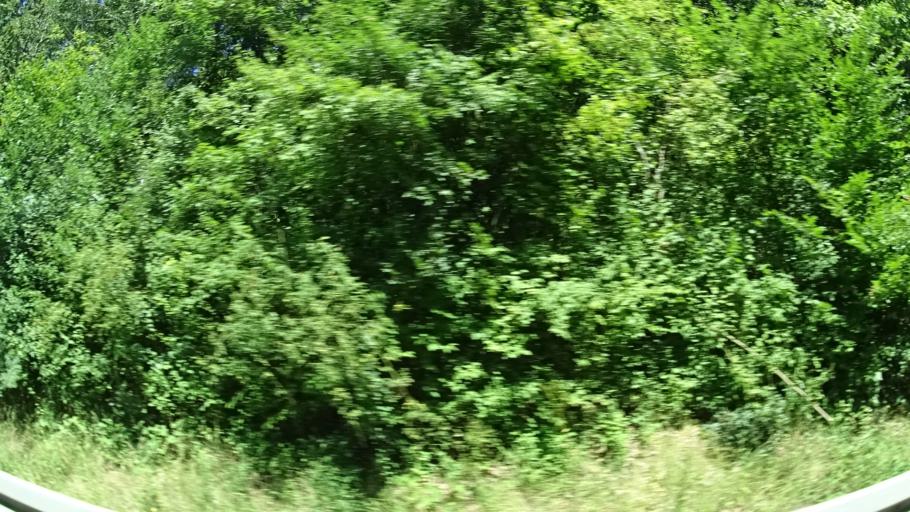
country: DE
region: Bavaria
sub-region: Regierungsbezirk Unterfranken
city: Guntersleben
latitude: 49.8726
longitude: 9.9211
